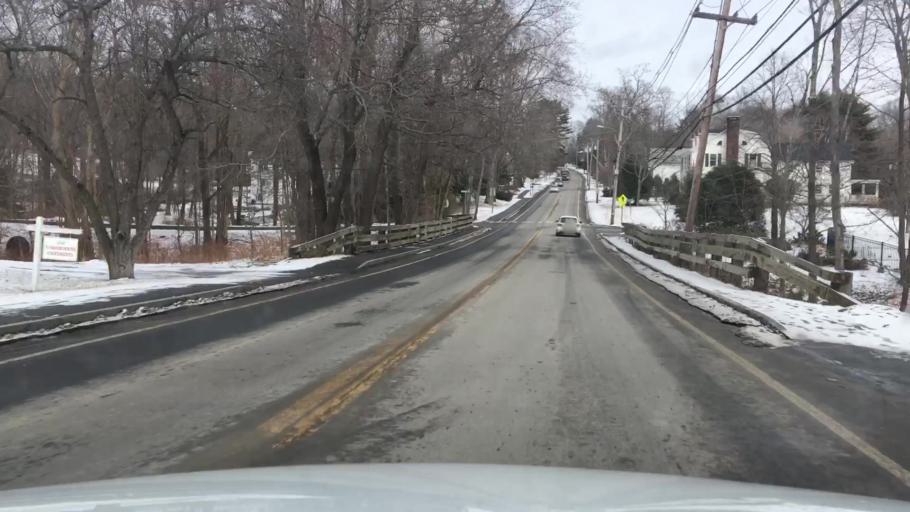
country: US
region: Maine
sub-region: Knox County
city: Camden
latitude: 44.2130
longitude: -69.0634
